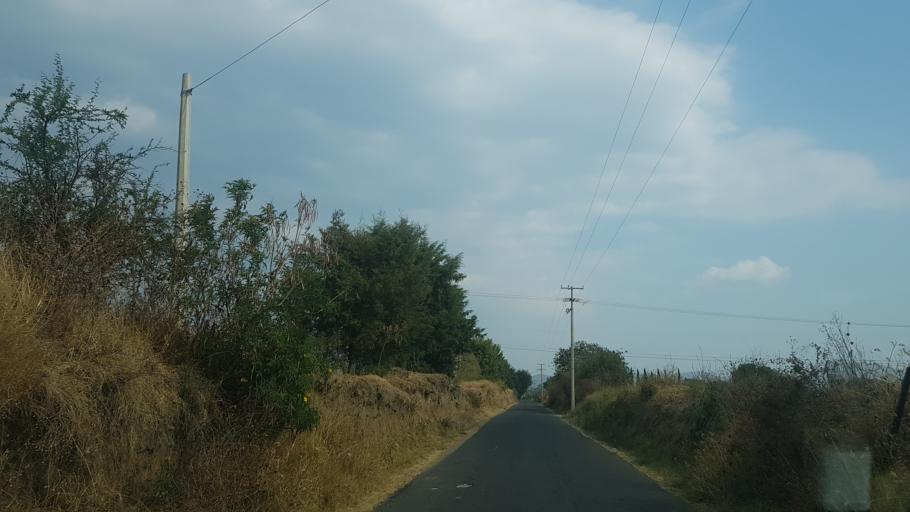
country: MX
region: Puebla
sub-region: Santa Isabel Cholula
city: Santa Ana Acozautla
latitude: 18.9545
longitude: -98.4001
